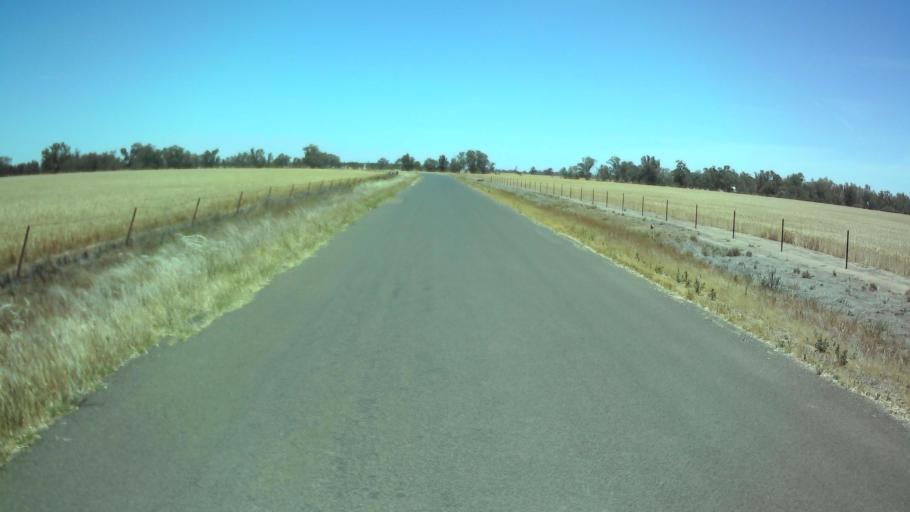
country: AU
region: New South Wales
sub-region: Weddin
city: Grenfell
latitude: -34.0335
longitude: 147.7901
